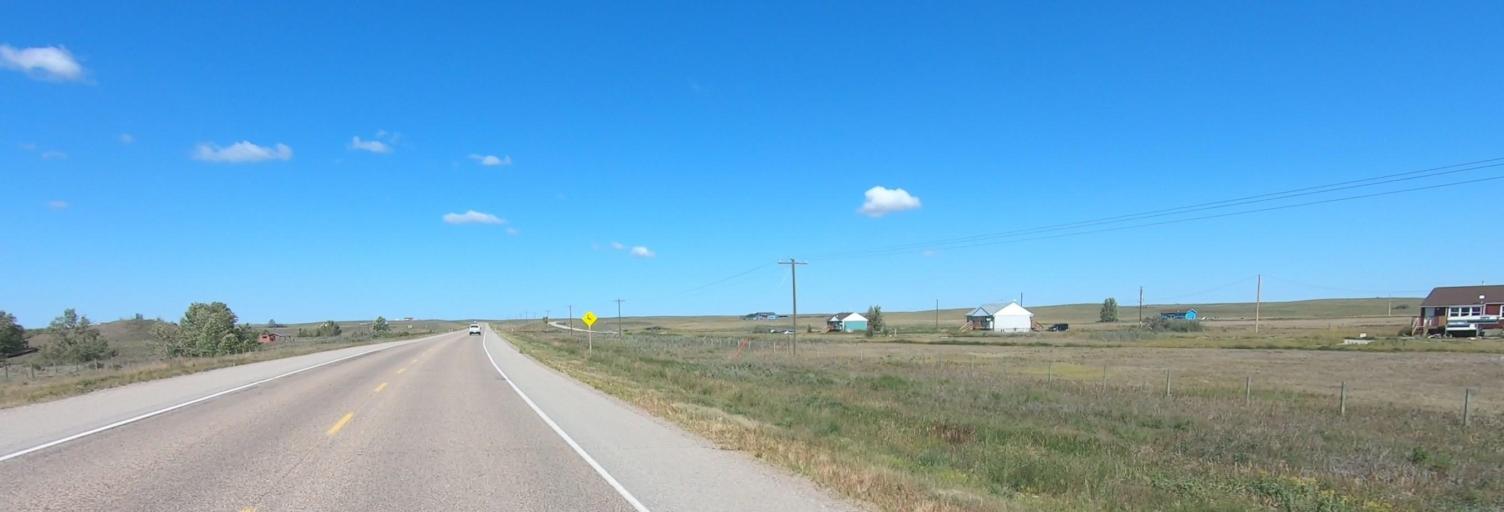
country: CA
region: Alberta
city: Strathmore
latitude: 50.8580
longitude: -113.1360
